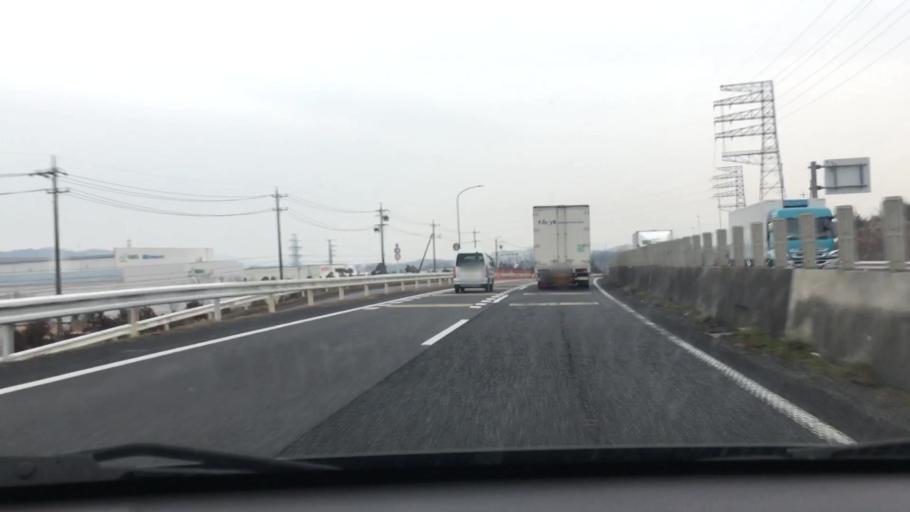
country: JP
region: Mie
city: Ueno-ebisumachi
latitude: 34.7238
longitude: 136.0859
